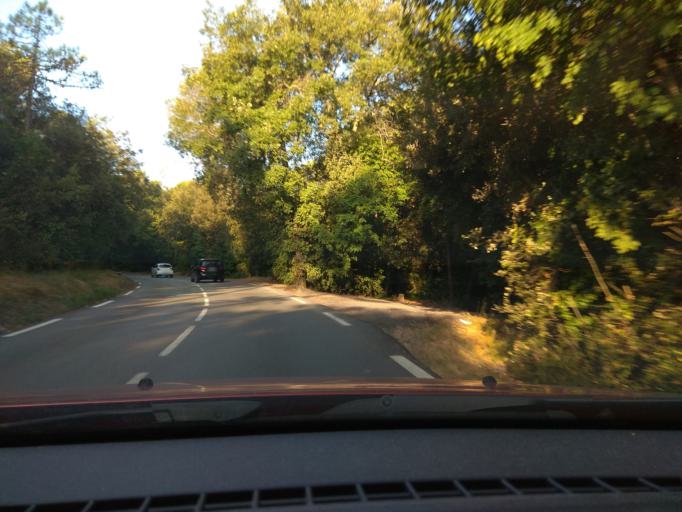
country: FR
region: Provence-Alpes-Cote d'Azur
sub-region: Departement des Alpes-Maritimes
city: Le Rouret
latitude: 43.6607
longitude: 7.0316
